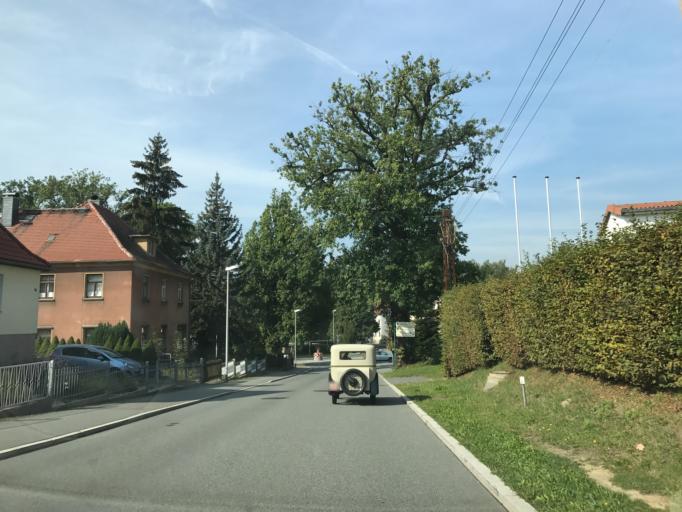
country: DE
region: Saxony
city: Lobau
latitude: 51.0911
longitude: 14.6751
